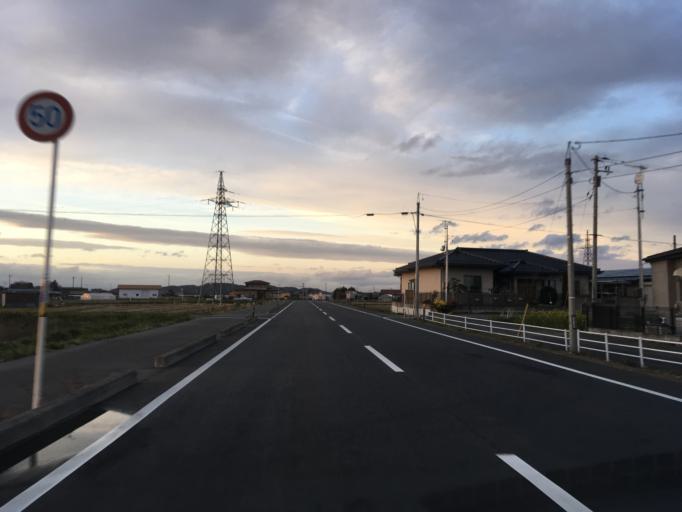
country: JP
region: Miyagi
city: Wakuya
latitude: 38.7099
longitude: 141.2594
